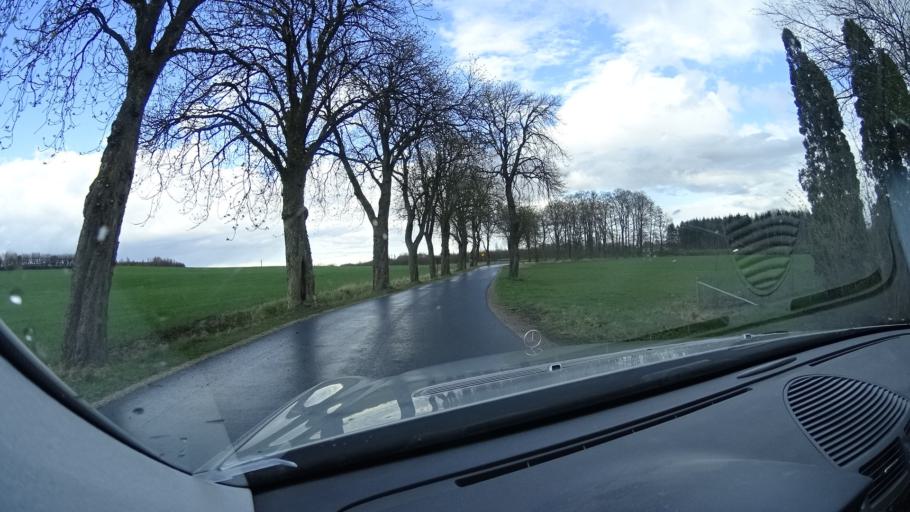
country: SE
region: Skane
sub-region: Eslovs Kommun
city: Eslov
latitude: 55.8149
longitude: 13.2922
